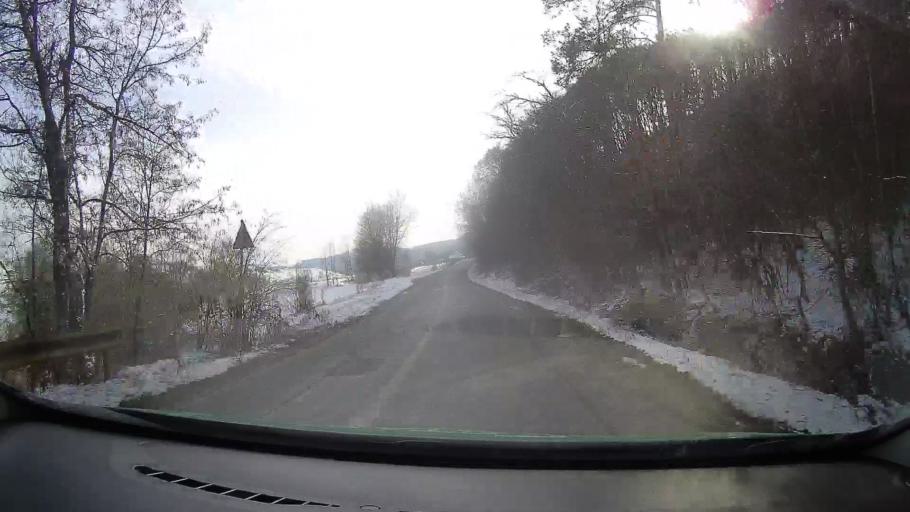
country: RO
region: Mures
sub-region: Comuna Apold
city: Saes
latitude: 46.1784
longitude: 24.7574
